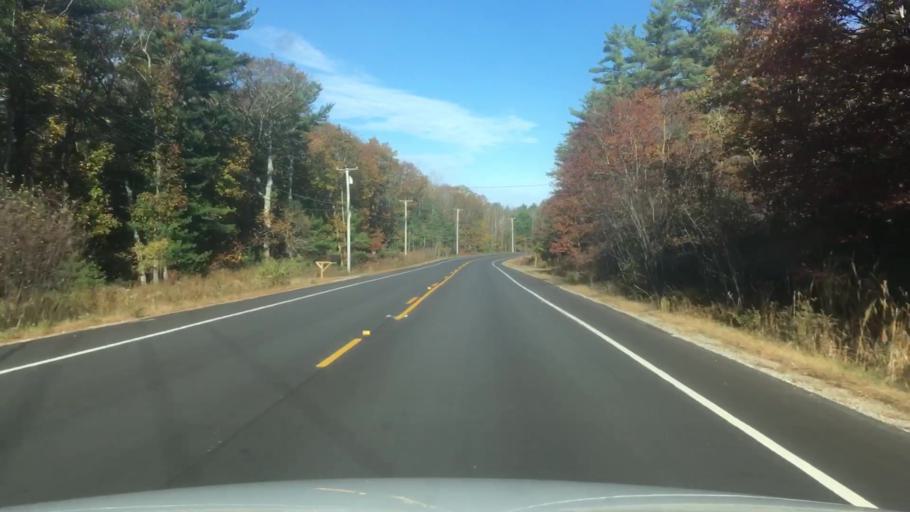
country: US
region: Maine
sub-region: Sagadahoc County
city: Woolwich
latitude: 43.8805
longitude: -69.7879
